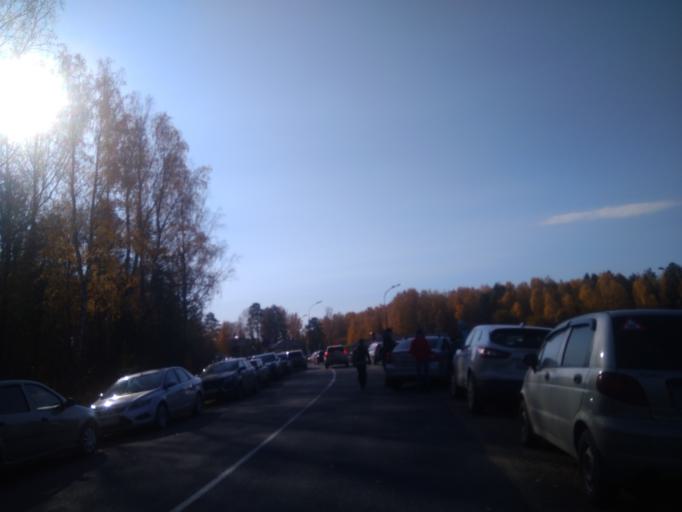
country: RU
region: Sverdlovsk
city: Mikhaylovsk
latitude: 56.5271
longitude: 59.2261
